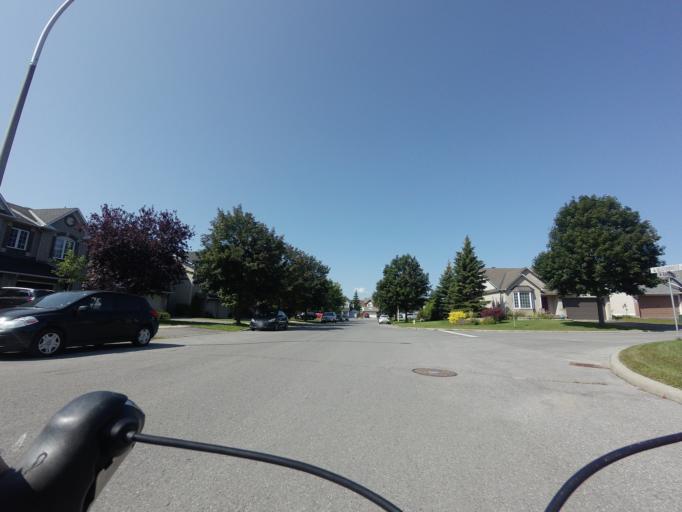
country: CA
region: Ontario
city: Bells Corners
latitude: 45.2799
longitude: -75.8452
